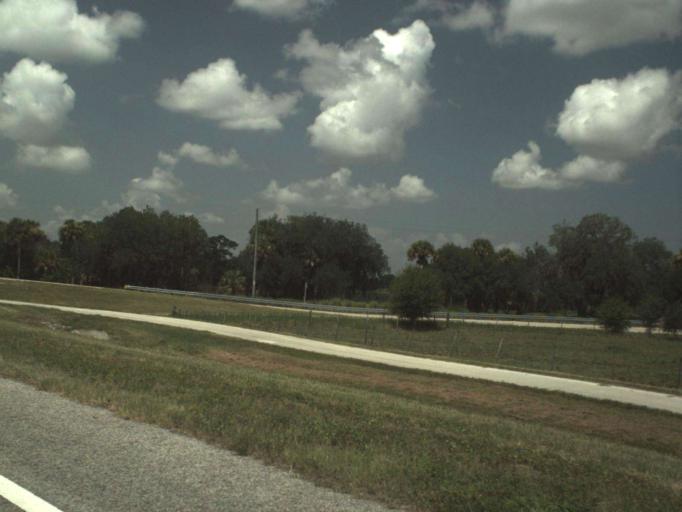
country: US
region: Florida
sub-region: Saint Lucie County
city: Fort Pierce South
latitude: 27.3991
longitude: -80.4551
